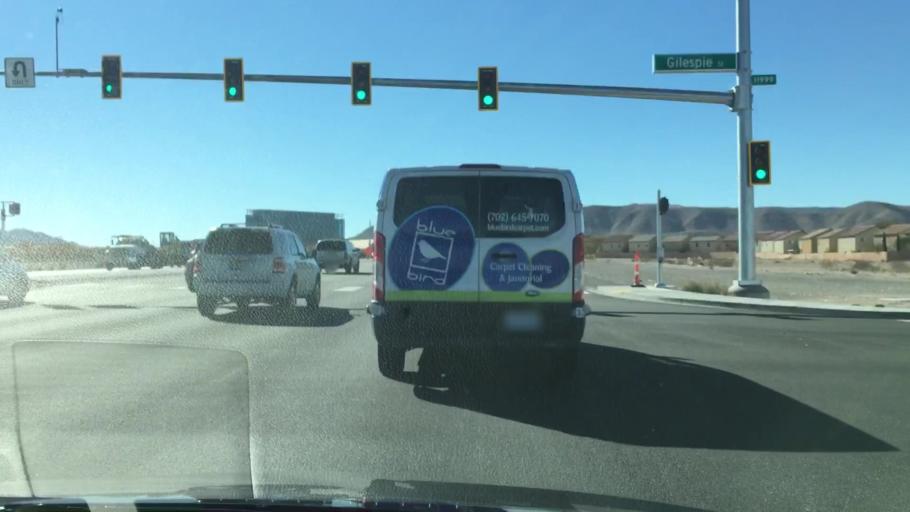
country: US
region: Nevada
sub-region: Clark County
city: Enterprise
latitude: 35.9728
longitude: -115.1627
